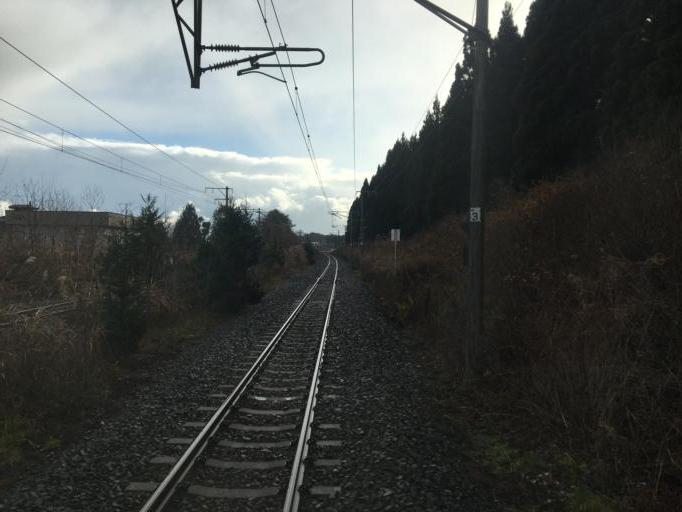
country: JP
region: Aomori
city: Aomori Shi
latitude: 40.9193
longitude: 141.0288
